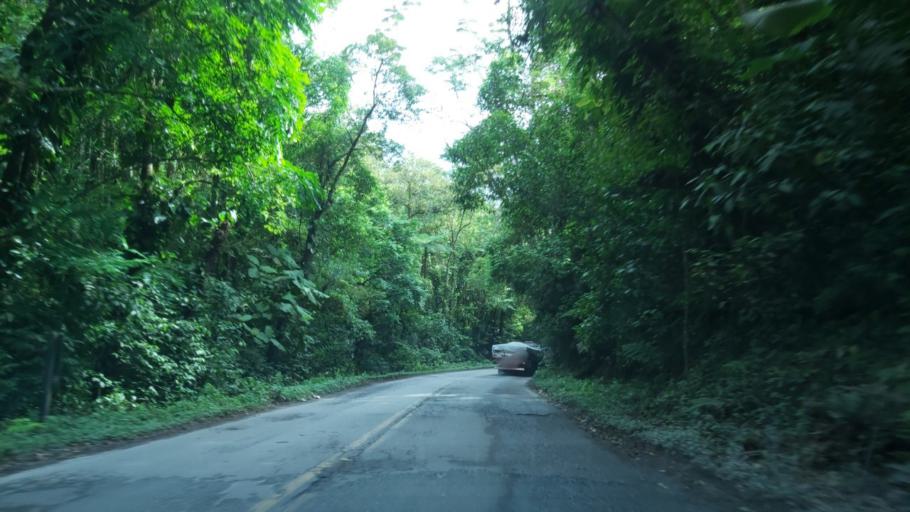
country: BR
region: Sao Paulo
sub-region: Miracatu
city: Miracatu
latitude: -24.0342
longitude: -47.5619
